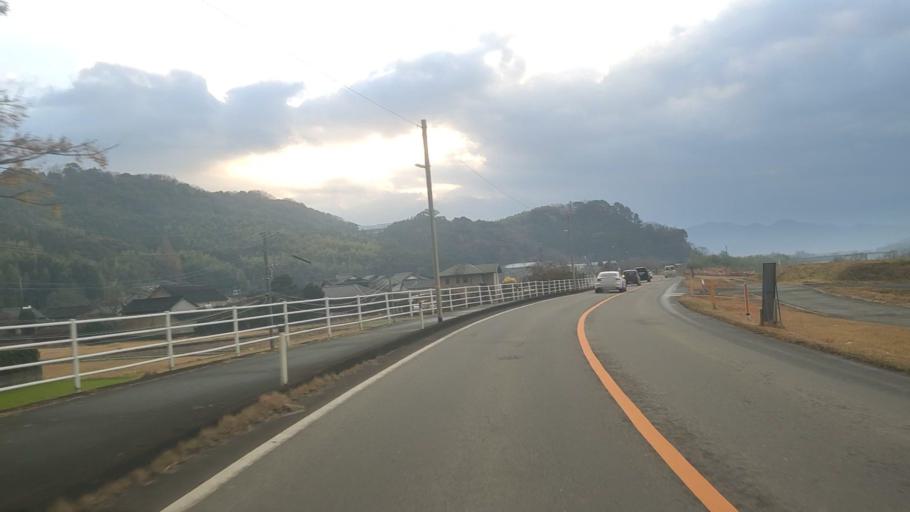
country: JP
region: Kumamoto
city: Uto
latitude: 32.7008
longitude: 130.7825
